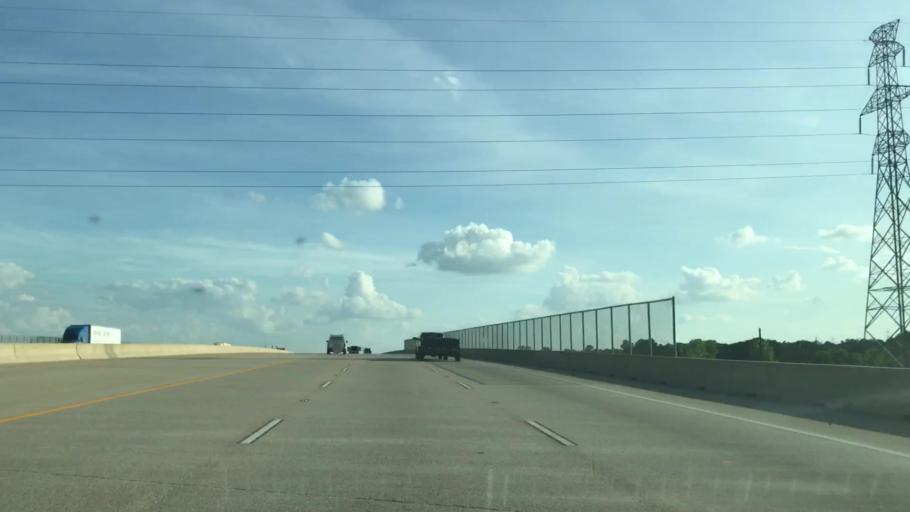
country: US
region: Texas
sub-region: Tarrant County
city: Euless
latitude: 32.8175
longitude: -97.0183
